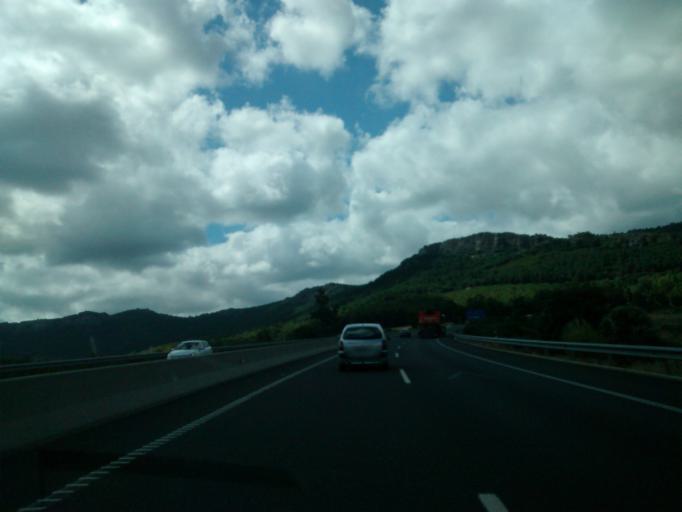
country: ES
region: Extremadura
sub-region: Provincia de Caceres
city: Higuera
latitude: 39.7059
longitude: -5.6898
